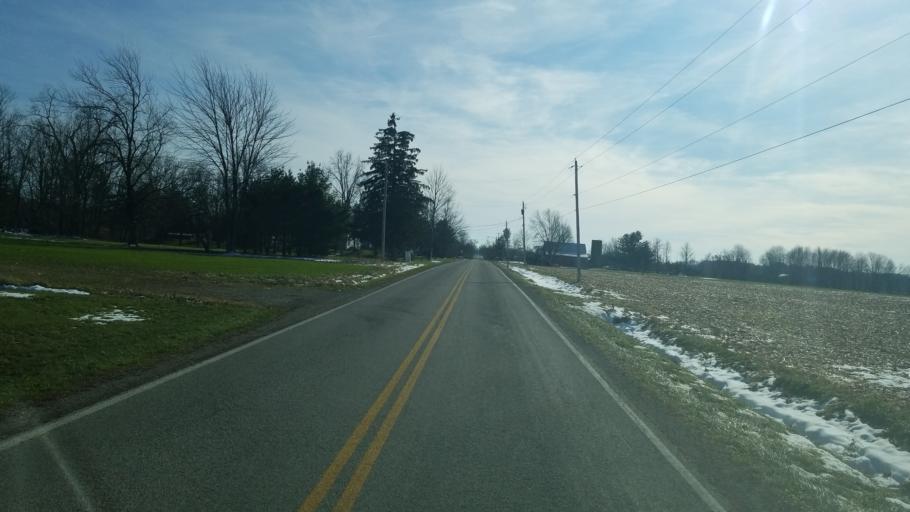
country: US
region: Ohio
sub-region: Huron County
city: Wakeman
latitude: 41.2279
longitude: -82.3610
